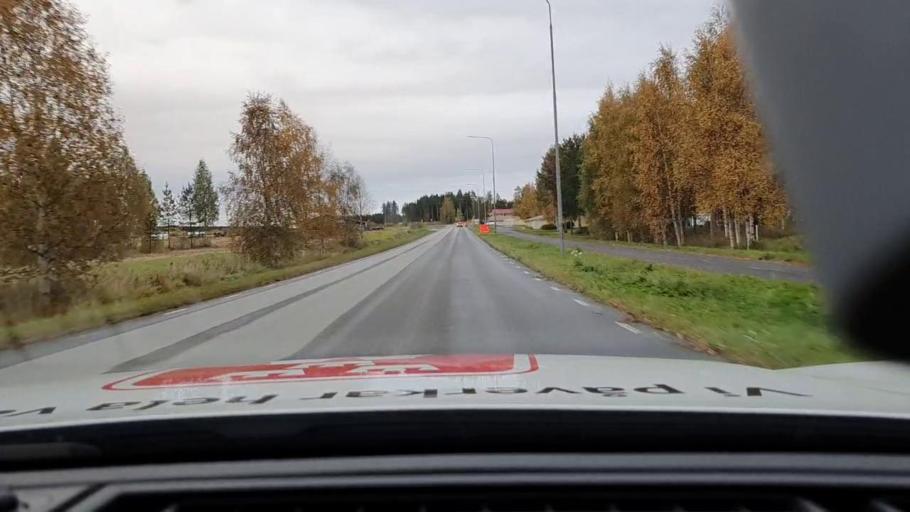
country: SE
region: Norrbotten
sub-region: Bodens Kommun
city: Saevast
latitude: 65.7565
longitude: 21.7563
